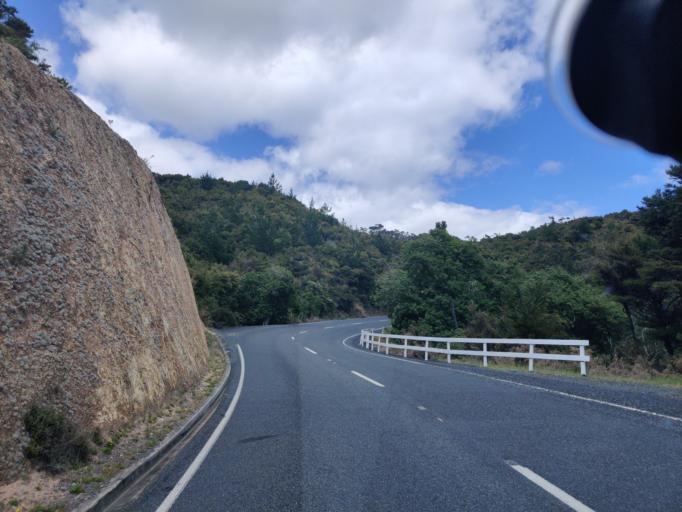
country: NZ
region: Northland
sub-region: Far North District
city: Paihia
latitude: -35.2602
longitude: 174.2227
